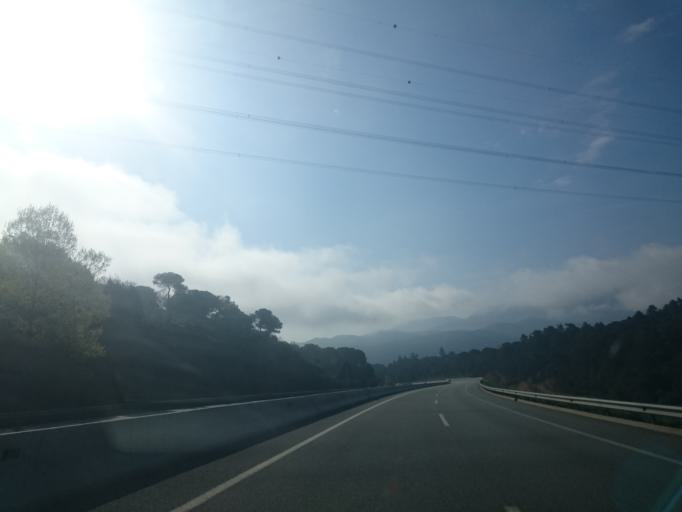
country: ES
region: Catalonia
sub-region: Provincia de Barcelona
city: Sant Julia de Vilatorta
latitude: 41.8977
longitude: 2.3442
